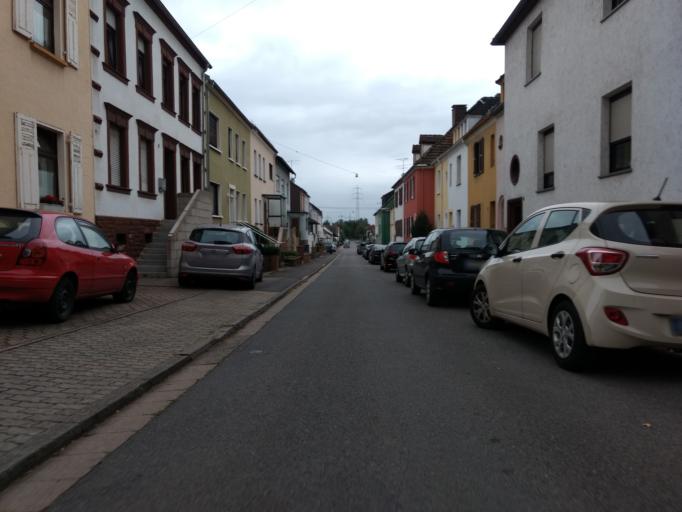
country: DE
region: Saarland
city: Nalbach
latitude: 49.3705
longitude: 6.7577
